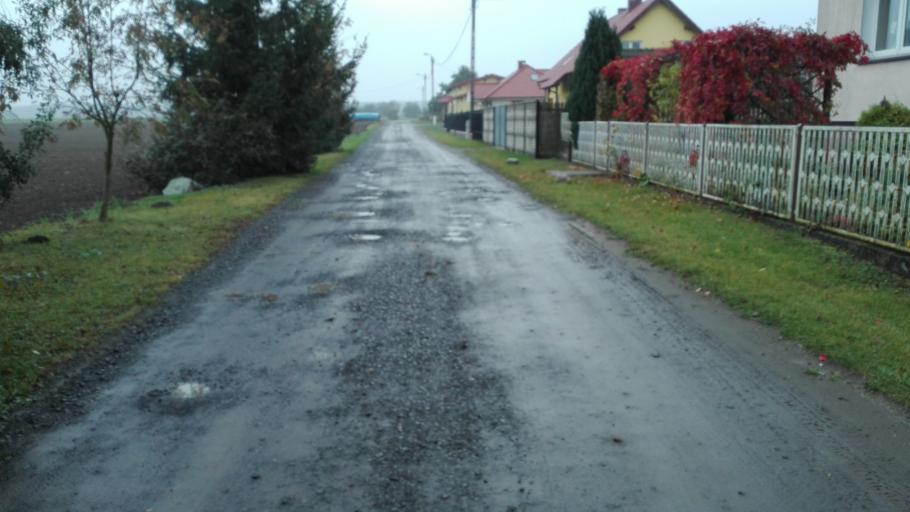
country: PL
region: Lubusz
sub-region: Powiat zielonogorski
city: Sulechow
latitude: 52.1266
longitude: 15.6906
